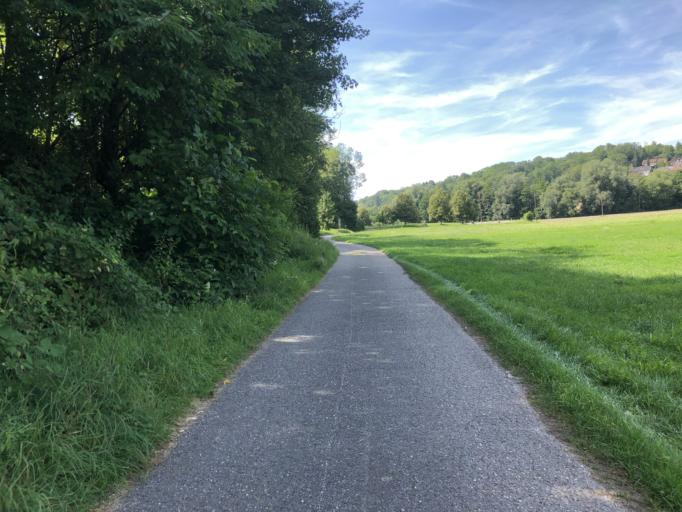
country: DE
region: Baden-Wuerttemberg
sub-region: Regierungsbezirk Stuttgart
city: Kirchberg an der Murr
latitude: 48.9374
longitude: 9.3345
